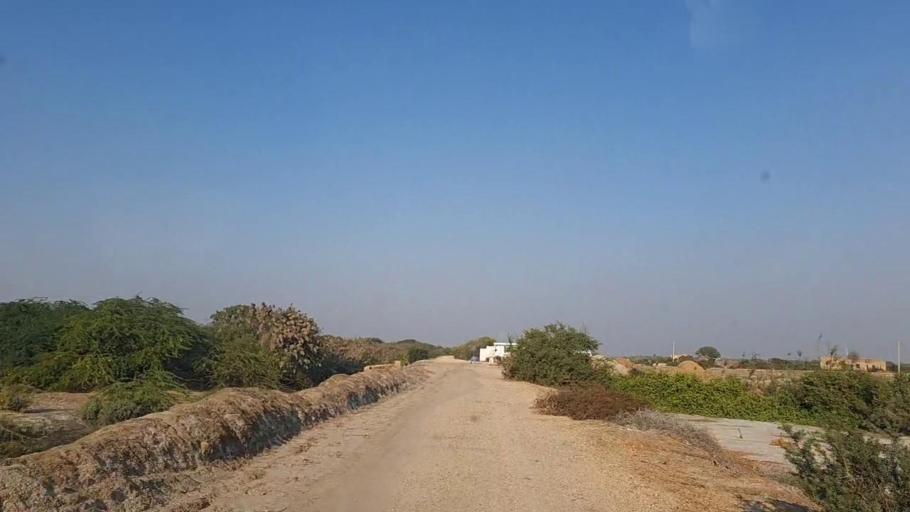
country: PK
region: Sindh
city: Thatta
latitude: 24.7255
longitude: 67.9489
